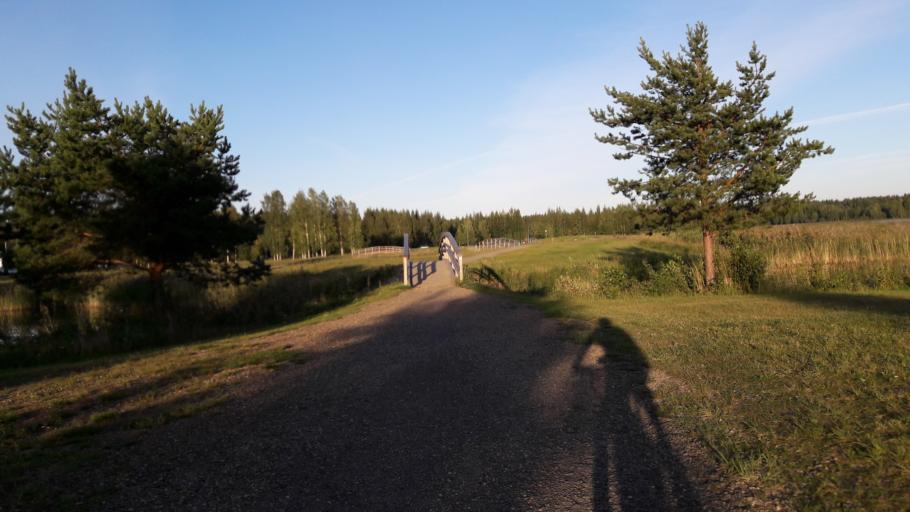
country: FI
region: North Karelia
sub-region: Joensuu
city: Joensuu
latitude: 62.6130
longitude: 29.7020
